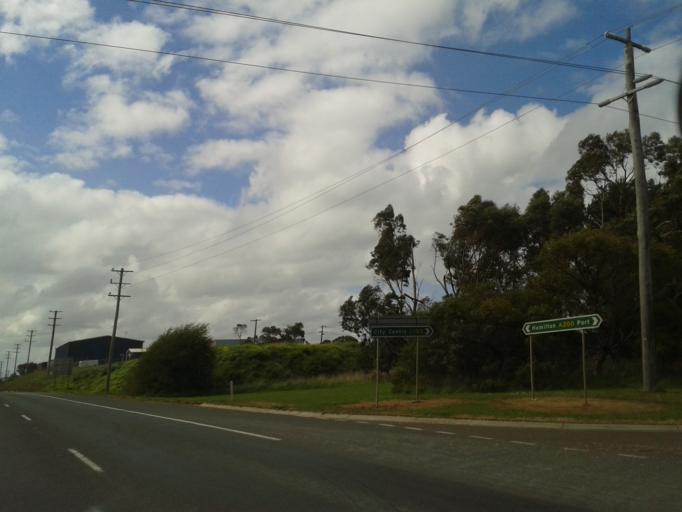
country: AU
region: Victoria
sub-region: Glenelg
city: Portland
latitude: -38.3394
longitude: 141.5873
